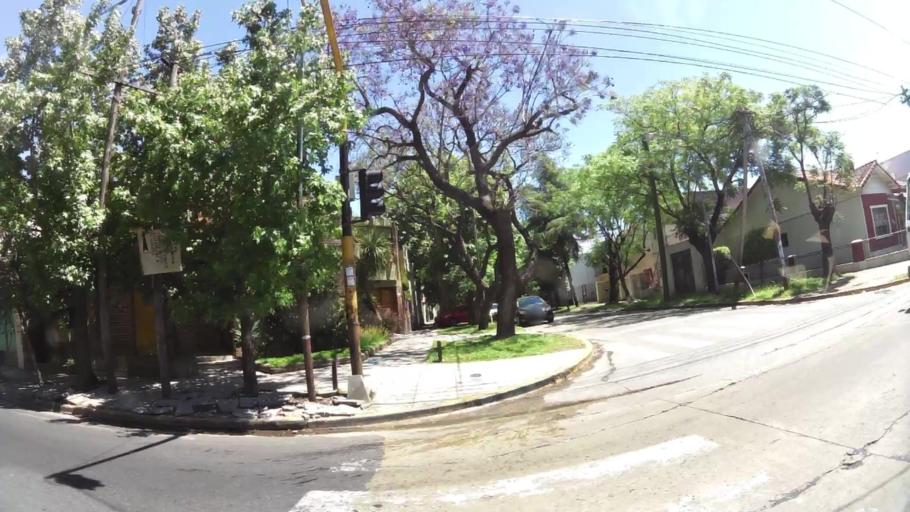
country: AR
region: Buenos Aires
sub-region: Partido de General San Martin
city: General San Martin
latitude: -34.5575
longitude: -58.5352
